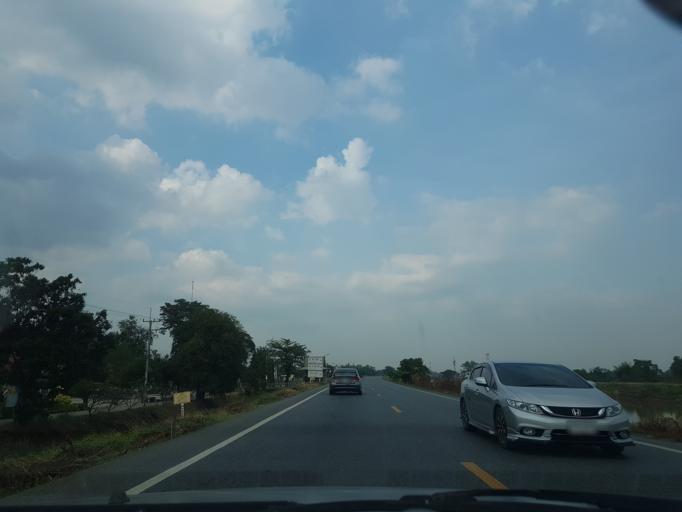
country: TH
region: Phra Nakhon Si Ayutthaya
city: Phachi
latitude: 14.4899
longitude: 100.7370
